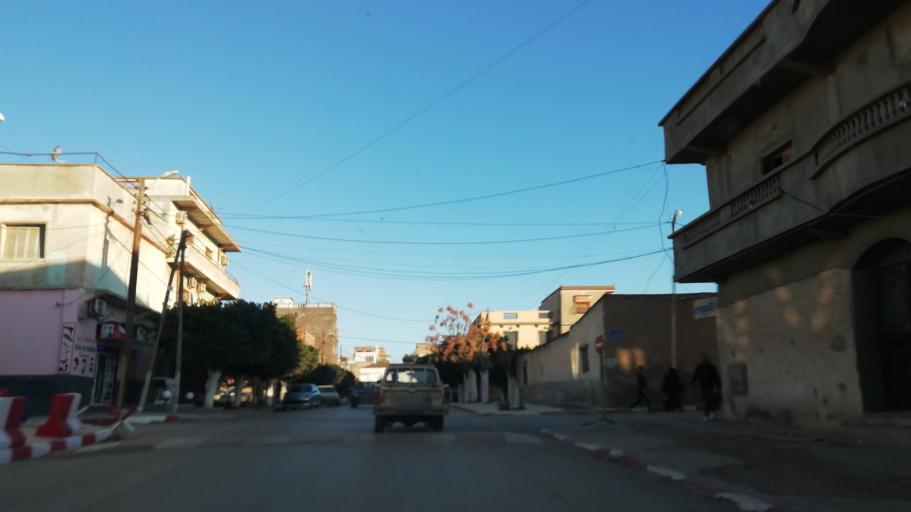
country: DZ
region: Oran
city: Sidi ech Chahmi
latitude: 35.6923
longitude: -0.5035
